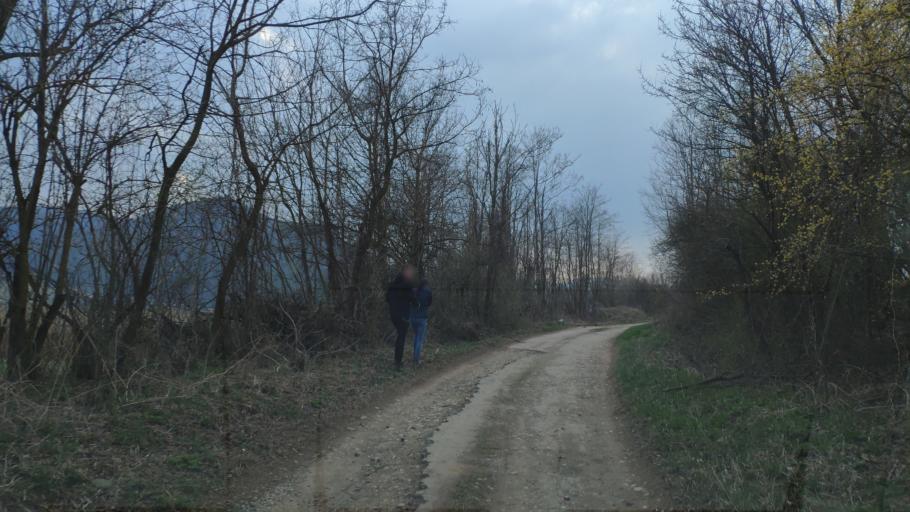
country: SK
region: Kosicky
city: Roznava
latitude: 48.6609
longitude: 20.3786
